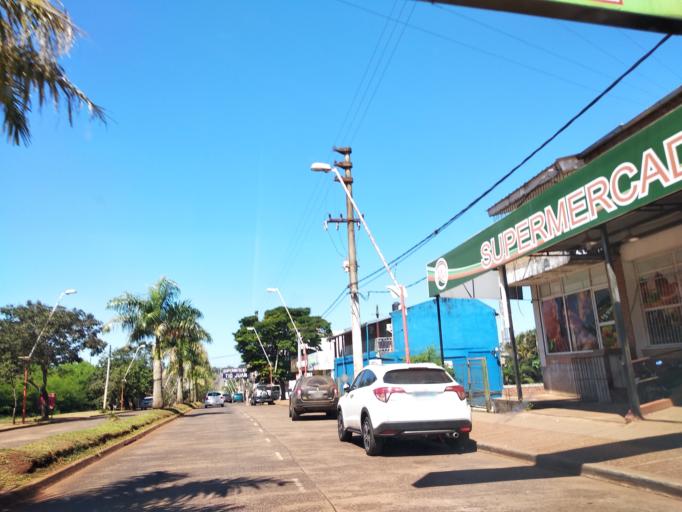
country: AR
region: Misiones
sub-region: Departamento de Iguazu
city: Puerto Iguazu
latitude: -25.6075
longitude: -54.5667
